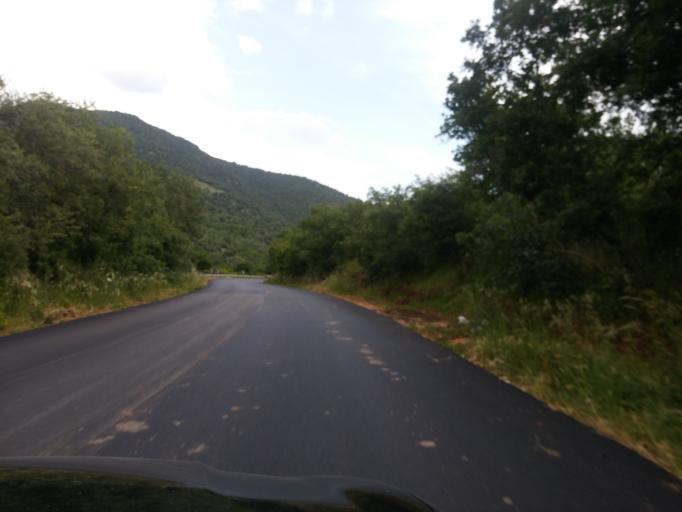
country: IT
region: Apulia
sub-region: Provincia di Foggia
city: Rignano Garganico
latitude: 41.7198
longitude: 15.5704
